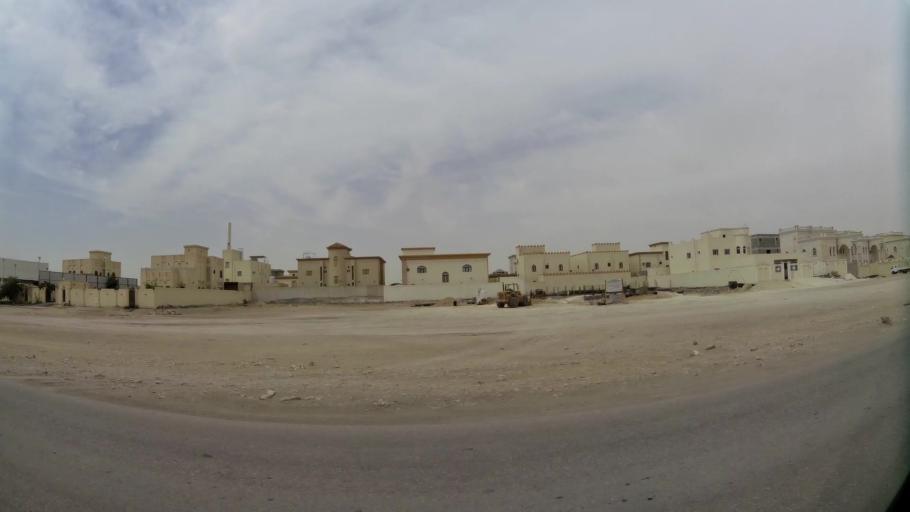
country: QA
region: Baladiyat ar Rayyan
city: Ar Rayyan
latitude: 25.2060
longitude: 51.4581
